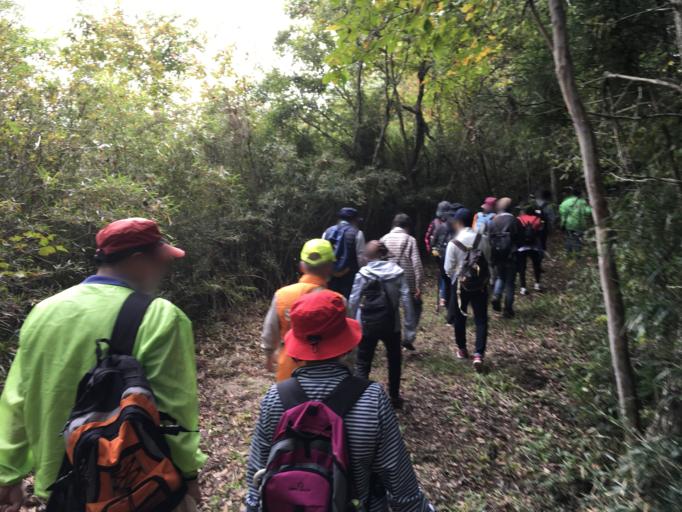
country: JP
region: Iwate
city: Ichinoseki
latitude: 38.8863
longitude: 141.0860
